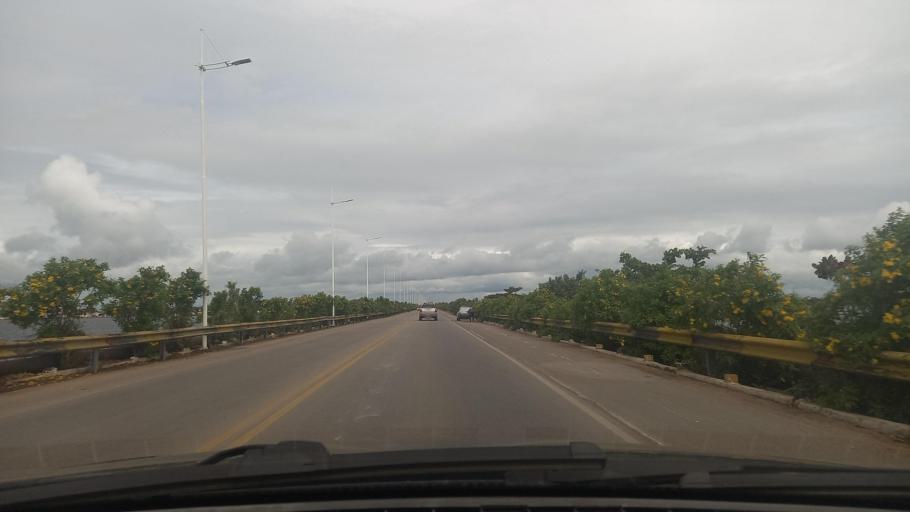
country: BR
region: Bahia
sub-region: Paulo Afonso
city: Paulo Afonso
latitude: -9.4256
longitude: -38.2296
